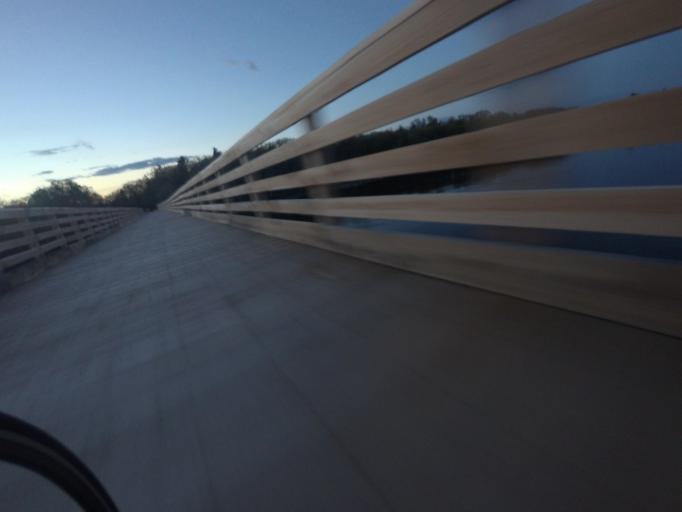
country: CA
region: Ontario
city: Arnprior
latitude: 45.4677
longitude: -76.2868
